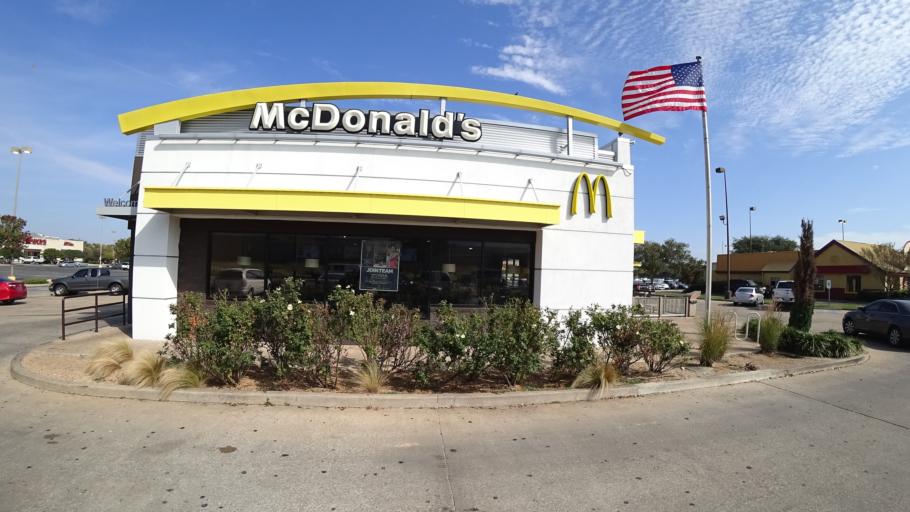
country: US
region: Texas
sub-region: Williamson County
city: Anderson Mill
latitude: 30.4596
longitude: -97.7926
